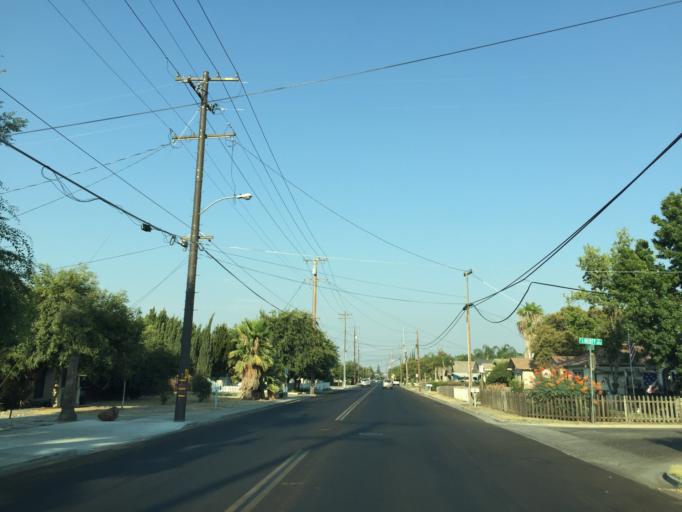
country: US
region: California
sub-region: Tulare County
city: Visalia
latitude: 36.3201
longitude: -119.2856
